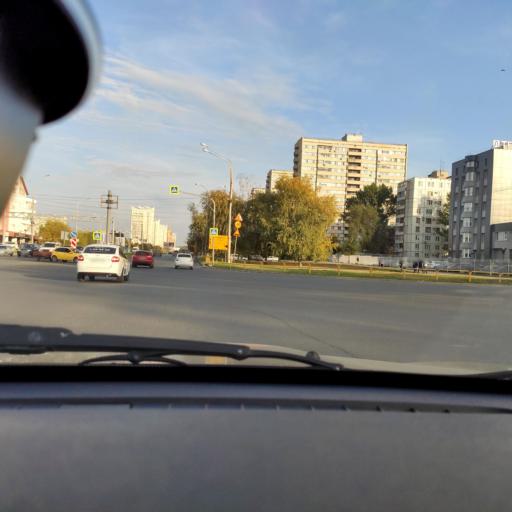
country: RU
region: Samara
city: Tol'yatti
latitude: 53.5149
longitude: 49.2779
